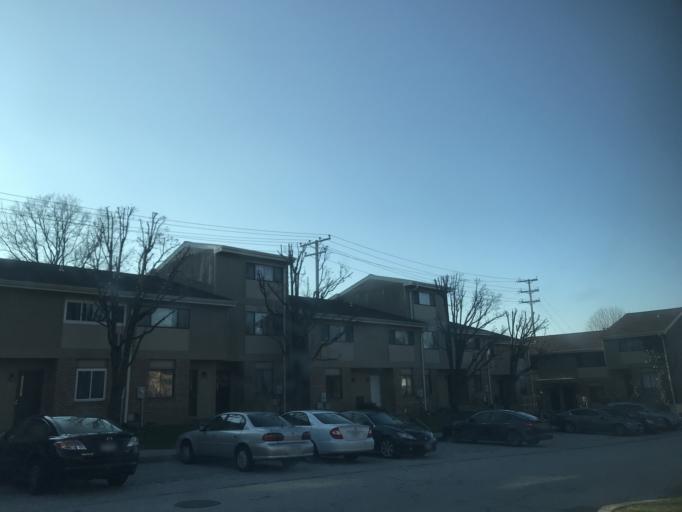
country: US
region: Maryland
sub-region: Baltimore County
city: Towson
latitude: 39.3979
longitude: -76.5944
